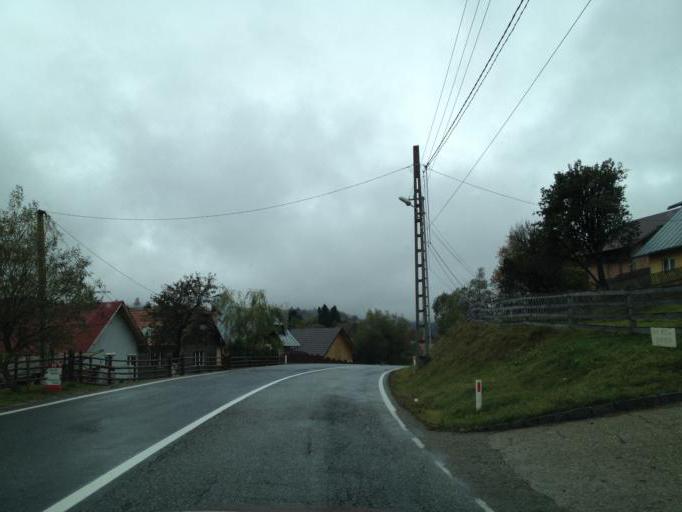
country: RO
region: Brasov
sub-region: Municipiul Brasov
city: Moeciu de Jos
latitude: 45.4729
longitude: 25.2979
